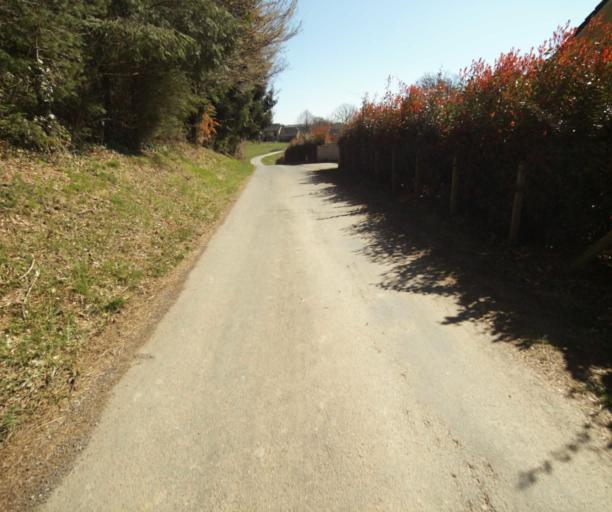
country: FR
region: Limousin
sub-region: Departement de la Correze
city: Saint-Clement
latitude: 45.3381
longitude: 1.6578
